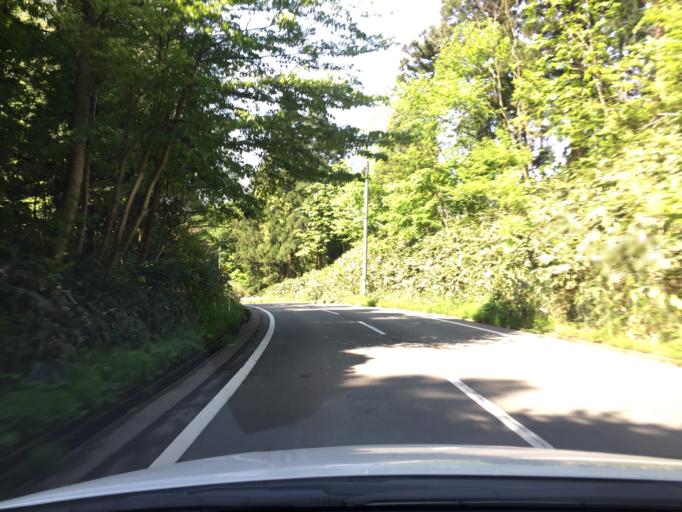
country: JP
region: Niigata
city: Kamo
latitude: 37.5597
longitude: 139.0788
